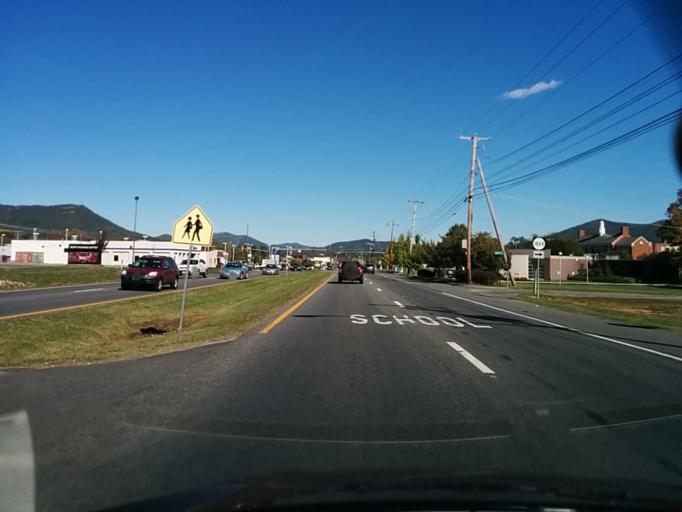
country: US
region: Virginia
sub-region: Roanoke County
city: Hollins
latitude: 37.3440
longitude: -79.9644
